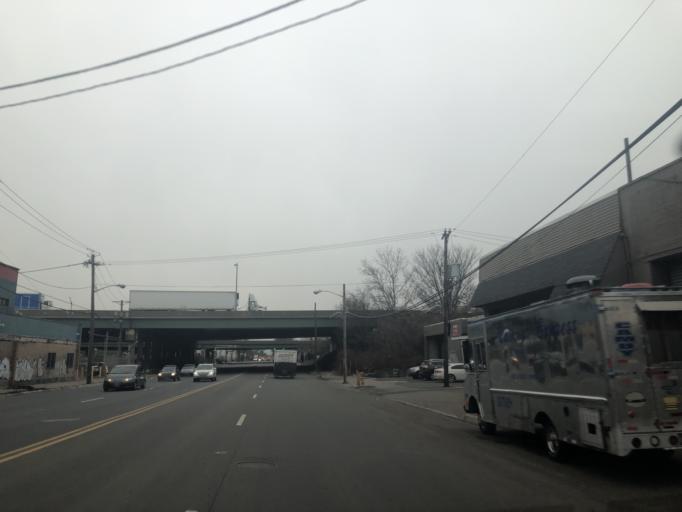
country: US
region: New Jersey
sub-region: Essex County
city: Newark
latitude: 40.7100
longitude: -74.1910
